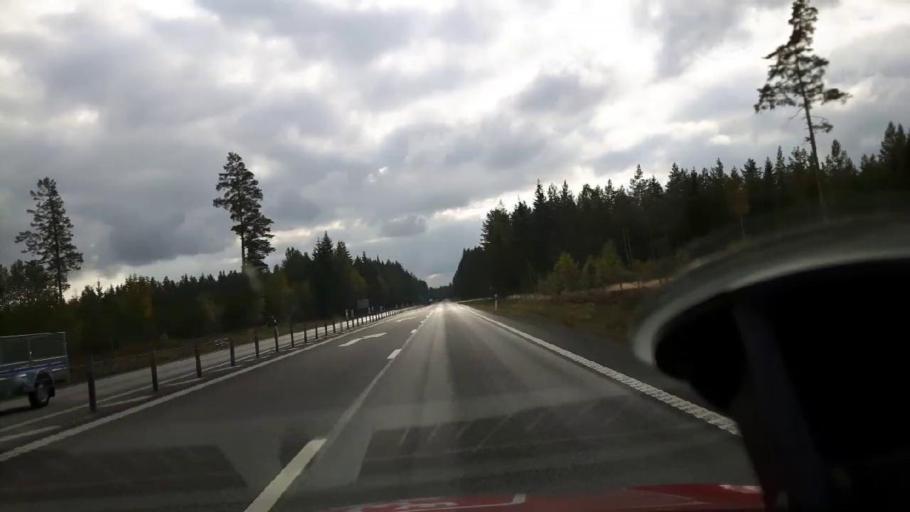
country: SE
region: Gaevleborg
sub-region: Gavle Kommun
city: Norrsundet
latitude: 61.0614
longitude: 16.9627
